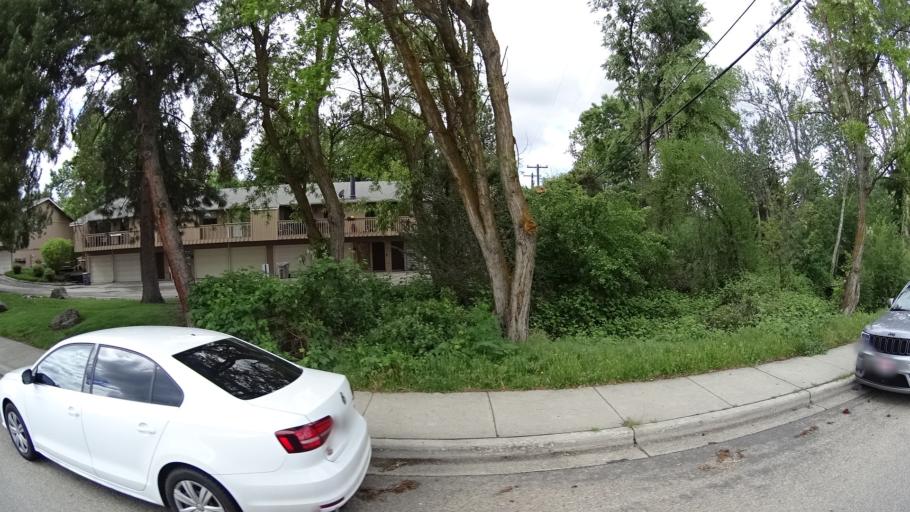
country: US
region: Idaho
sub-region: Ada County
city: Boise
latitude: 43.6492
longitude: -116.1934
